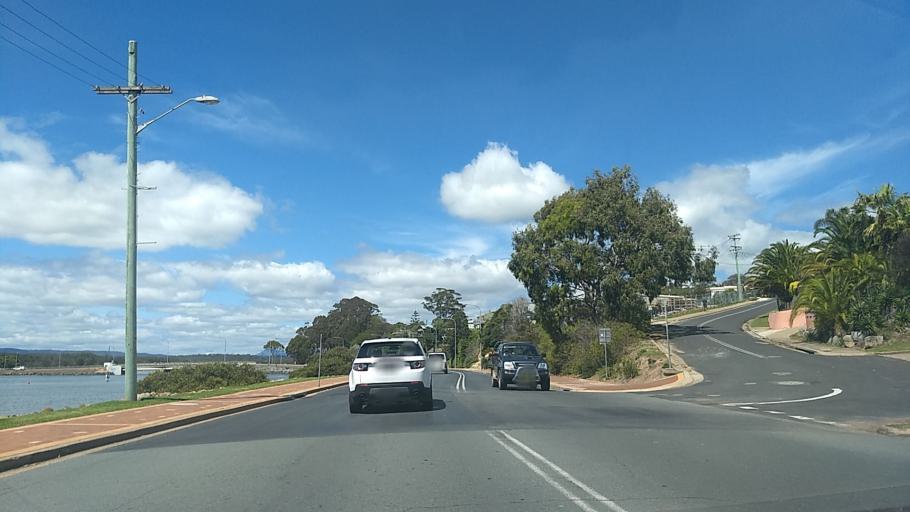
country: AU
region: New South Wales
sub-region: Bega Valley
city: Merimbula
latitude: -36.8914
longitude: 149.9104
